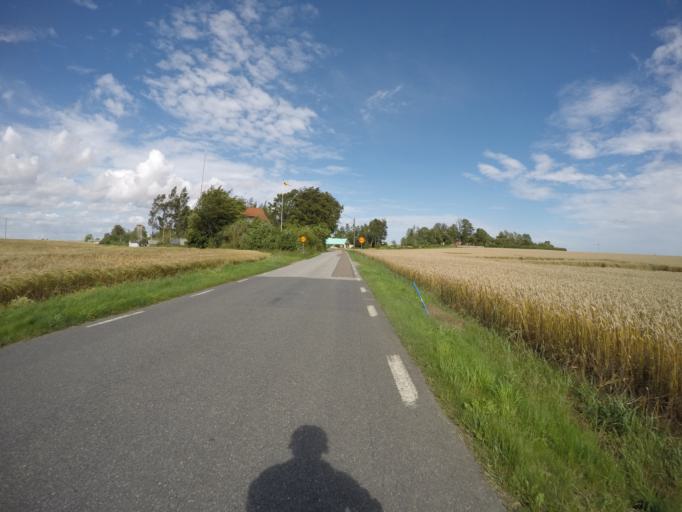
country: SE
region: Skane
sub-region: Simrishamns Kommun
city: Simrishamn
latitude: 55.4954
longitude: 14.2015
